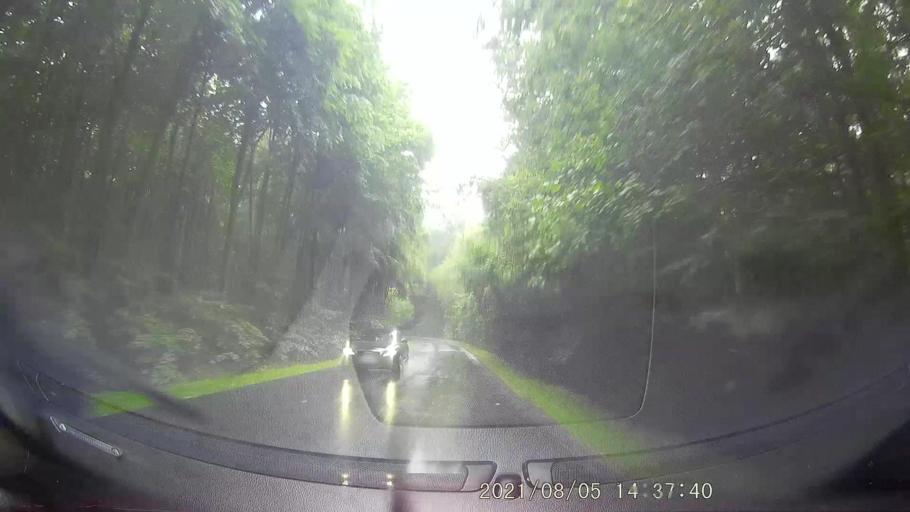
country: PL
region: Opole Voivodeship
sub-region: Powiat nyski
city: Sidzina
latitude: 50.4688
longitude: 17.4709
